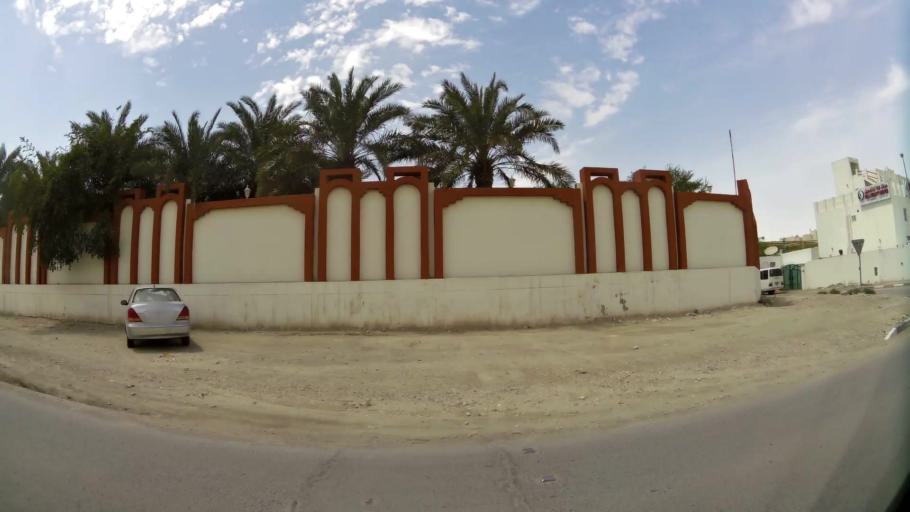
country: QA
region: Baladiyat ar Rayyan
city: Ar Rayyan
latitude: 25.2728
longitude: 51.4261
